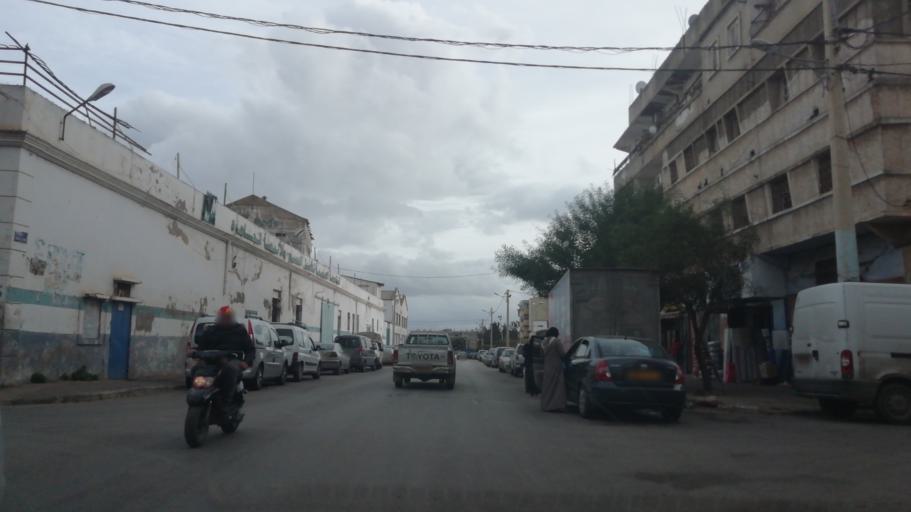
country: DZ
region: Oran
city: Oran
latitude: 35.6837
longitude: -0.6420
